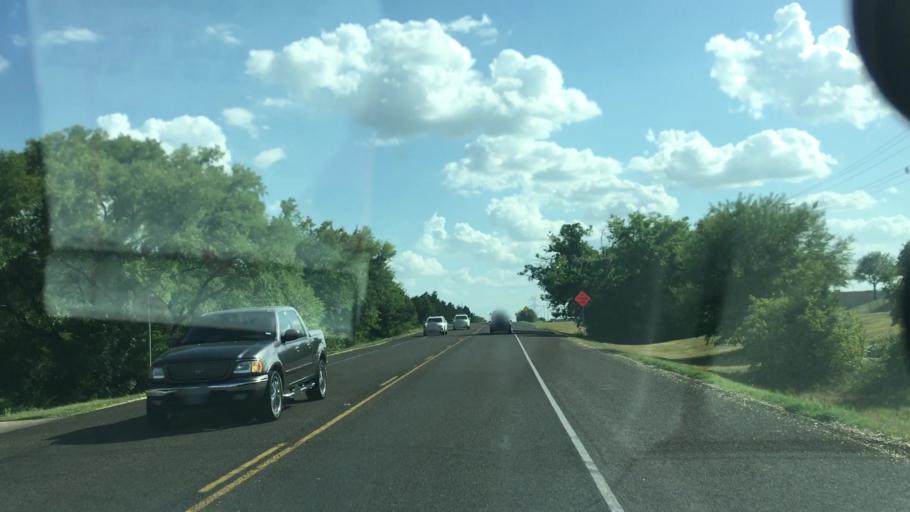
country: US
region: Texas
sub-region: Dallas County
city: Lancaster
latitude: 32.5649
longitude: -96.7658
